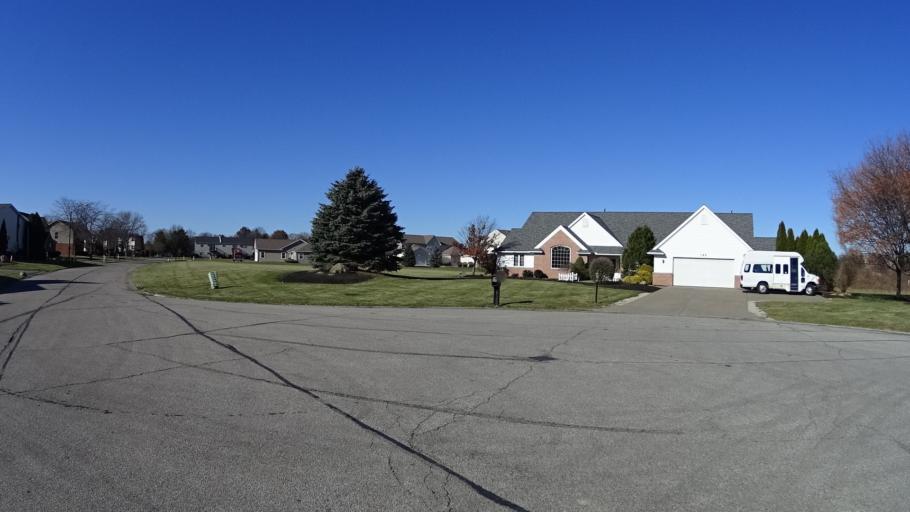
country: US
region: Ohio
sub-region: Lorain County
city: Elyria
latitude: 41.3609
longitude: -82.1532
